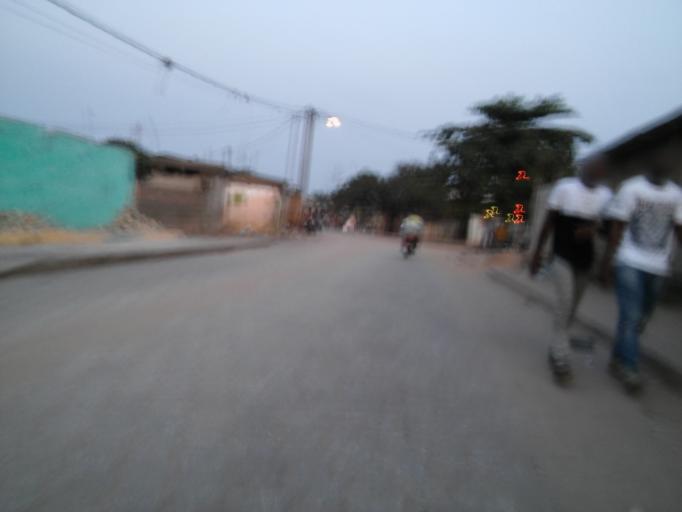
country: BJ
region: Atlantique
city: Abomey-Calavi
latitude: 6.3904
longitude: 2.3470
